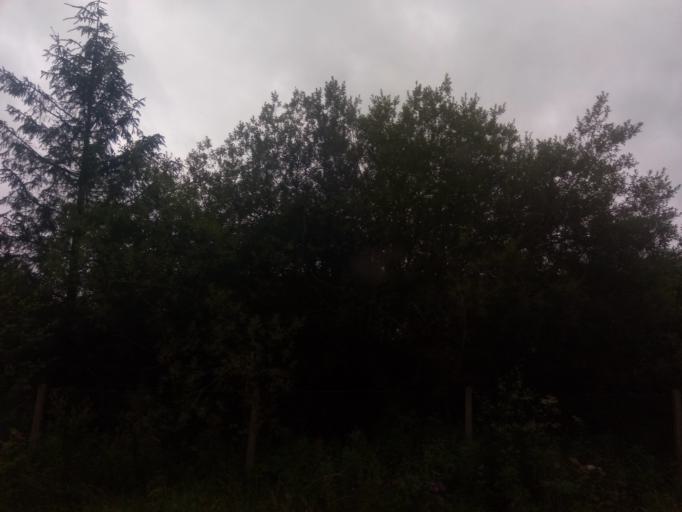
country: GB
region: England
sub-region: North Yorkshire
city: Settle
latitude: 54.0172
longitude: -2.2562
